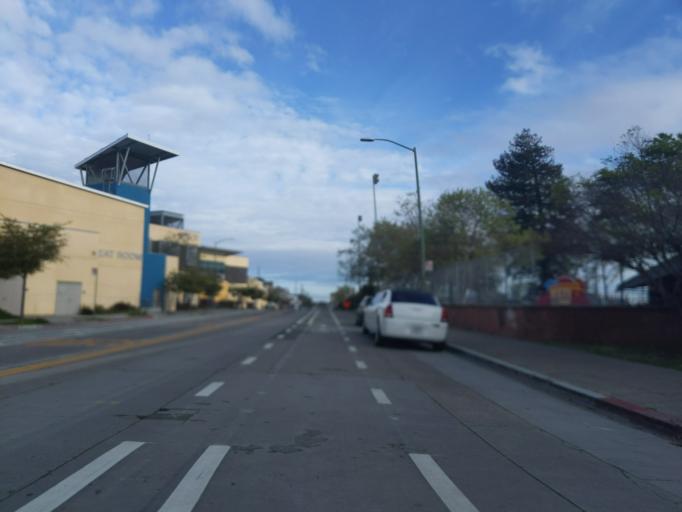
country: US
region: California
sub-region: Alameda County
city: Oakland
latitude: 37.7957
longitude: -122.2590
